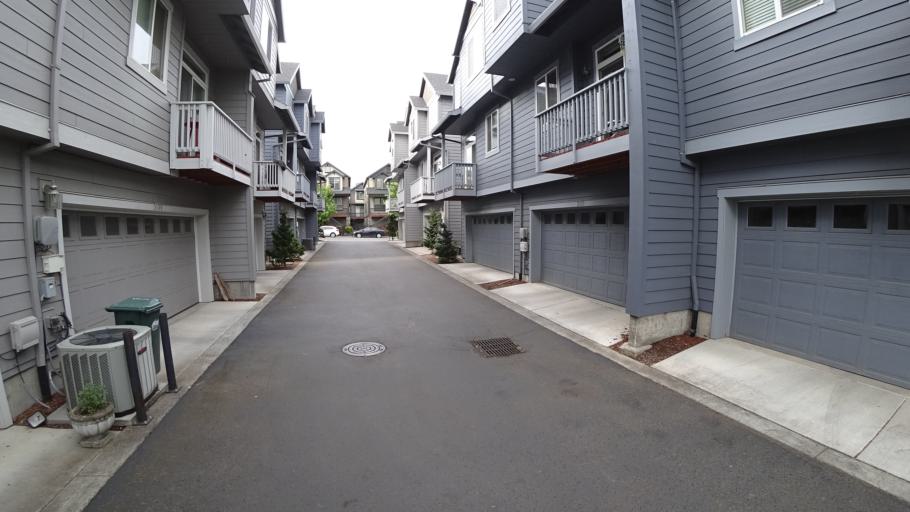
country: US
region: Oregon
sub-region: Washington County
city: Hillsboro
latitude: 45.5470
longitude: -122.9668
